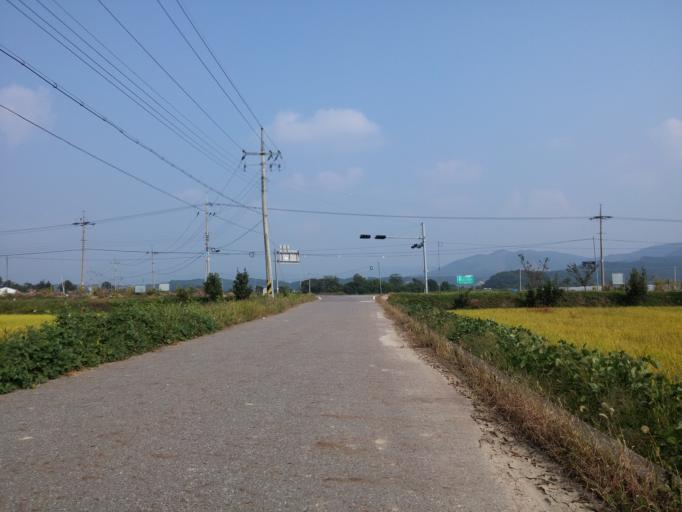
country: KR
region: Chungcheongbuk-do
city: Yong-dong
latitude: 36.3229
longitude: 127.7581
